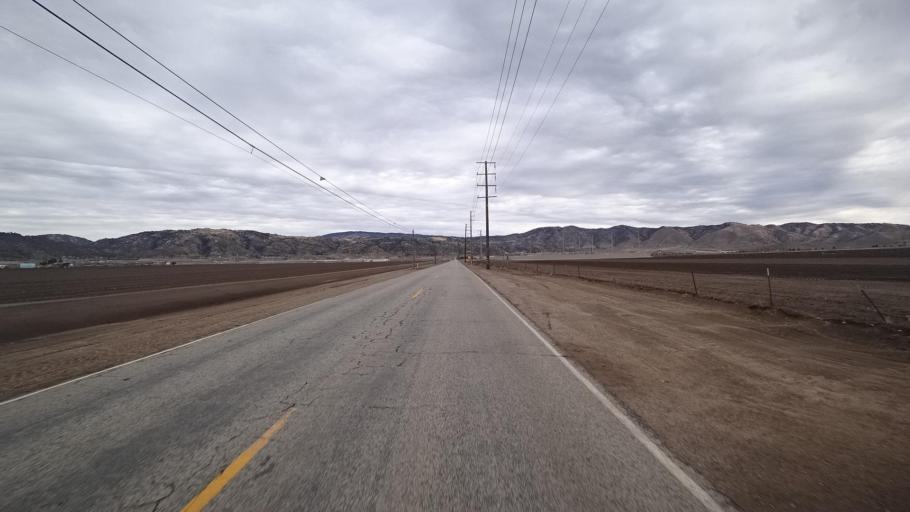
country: US
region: California
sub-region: Kern County
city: Stallion Springs
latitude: 35.0982
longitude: -118.6022
